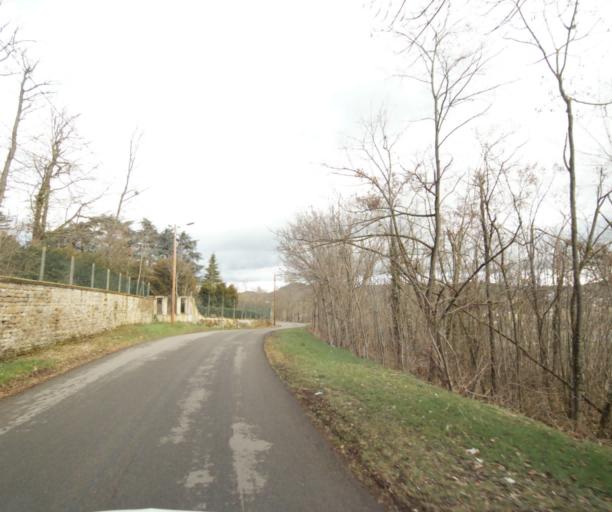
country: FR
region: Rhone-Alpes
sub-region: Departement de la Loire
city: La Talaudiere
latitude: 45.4715
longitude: 4.4202
